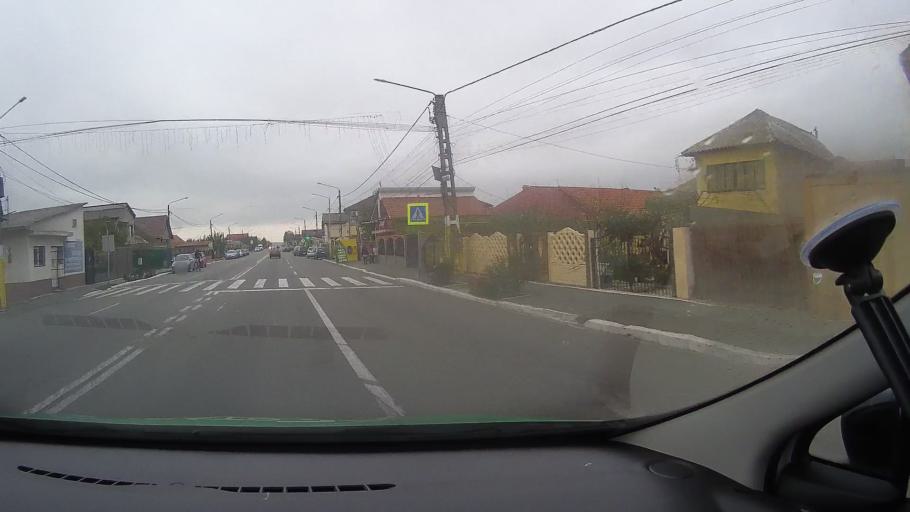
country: RO
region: Constanta
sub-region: Comuna Valu lui Traian
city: Valu lui Traian
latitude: 44.1666
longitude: 28.4592
